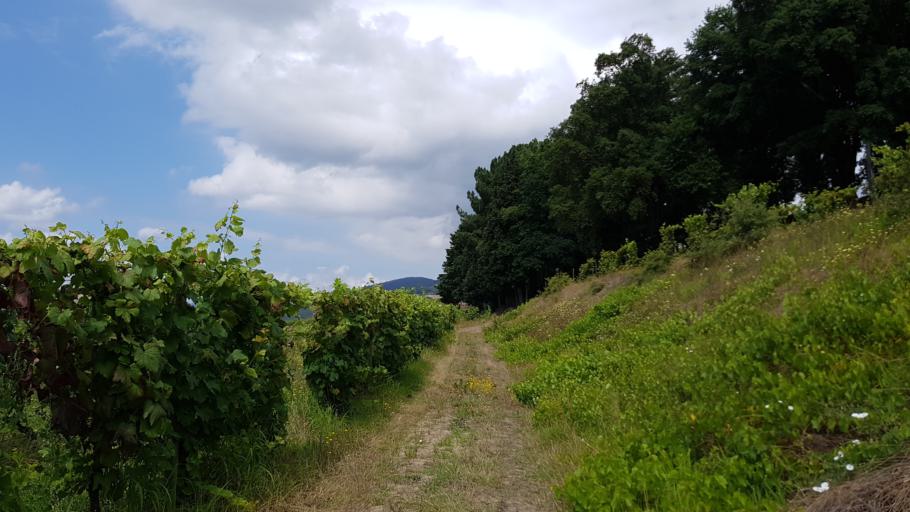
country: PT
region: Vila Real
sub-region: Mesao Frio
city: Mesao Frio
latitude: 41.1714
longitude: -7.8449
